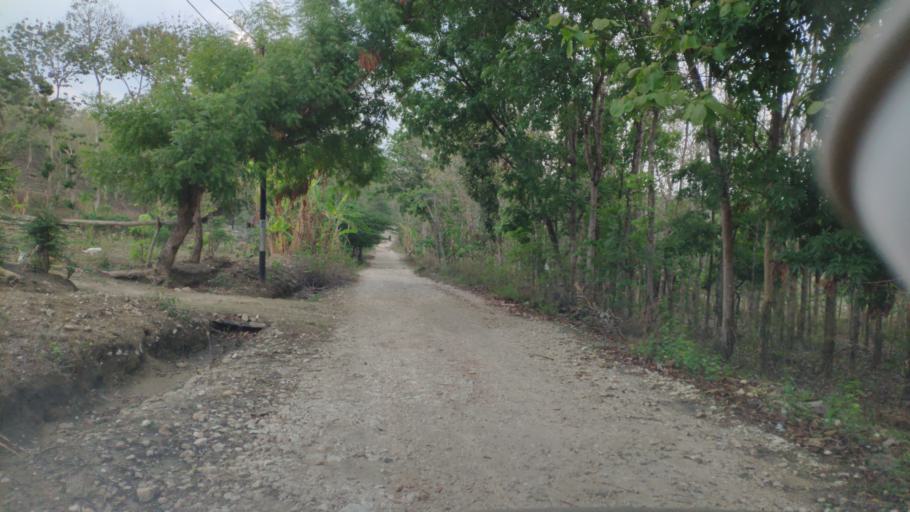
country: ID
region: Central Java
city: Semanggi
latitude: -7.0646
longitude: 111.4247
